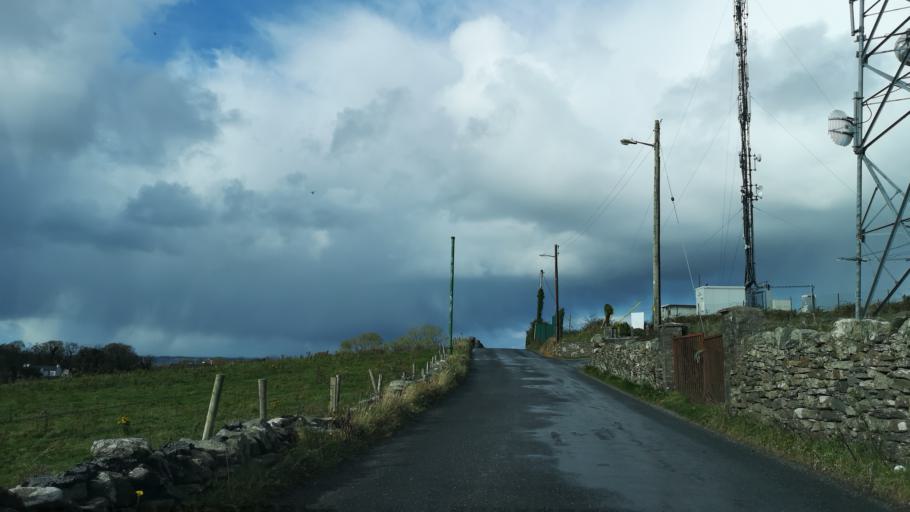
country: IE
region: Connaught
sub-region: Maigh Eo
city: Westport
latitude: 53.7954
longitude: -9.5188
